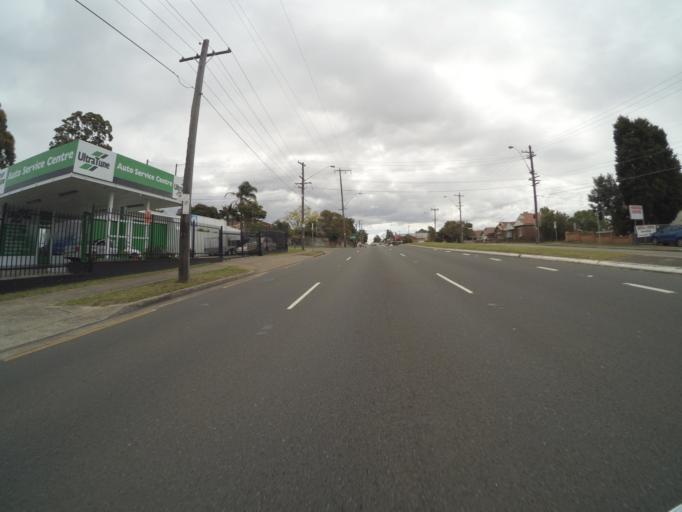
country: AU
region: New South Wales
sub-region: Kogarah
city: Kogarah
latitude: -33.9802
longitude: 151.1072
